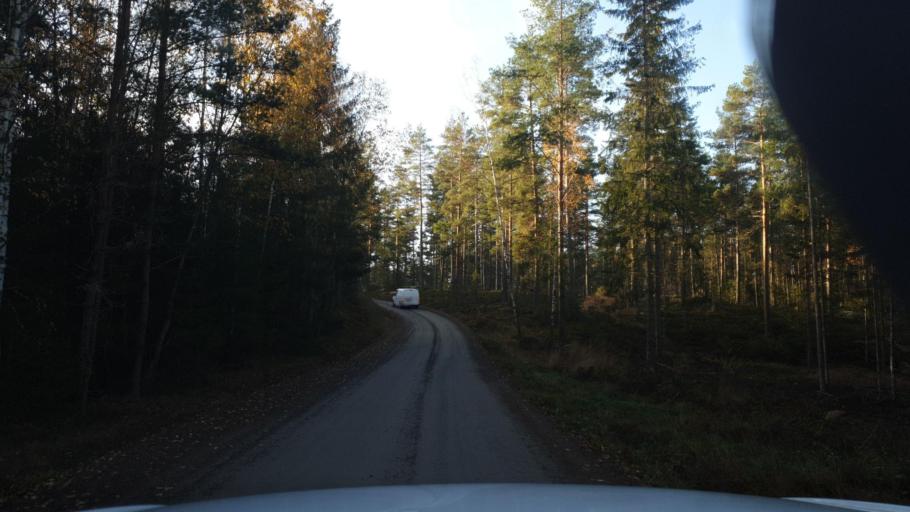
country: SE
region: Vaermland
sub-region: Grums Kommun
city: Grums
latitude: 59.4745
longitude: 12.9271
